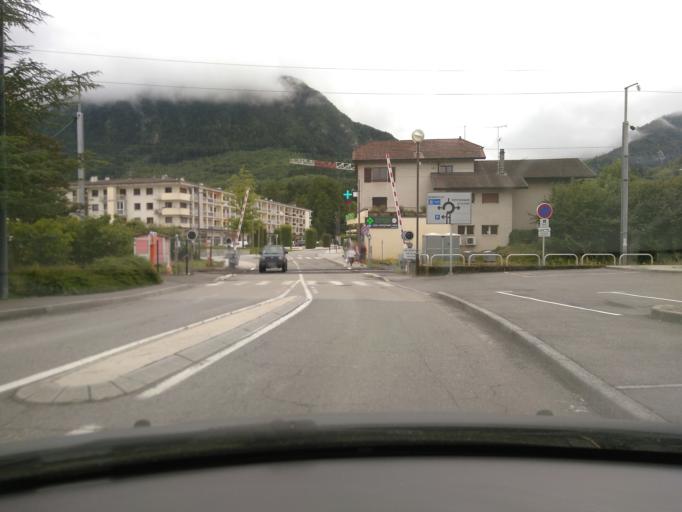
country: FR
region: Rhone-Alpes
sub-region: Departement de la Haute-Savoie
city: Bonneville
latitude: 46.0588
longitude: 6.3742
